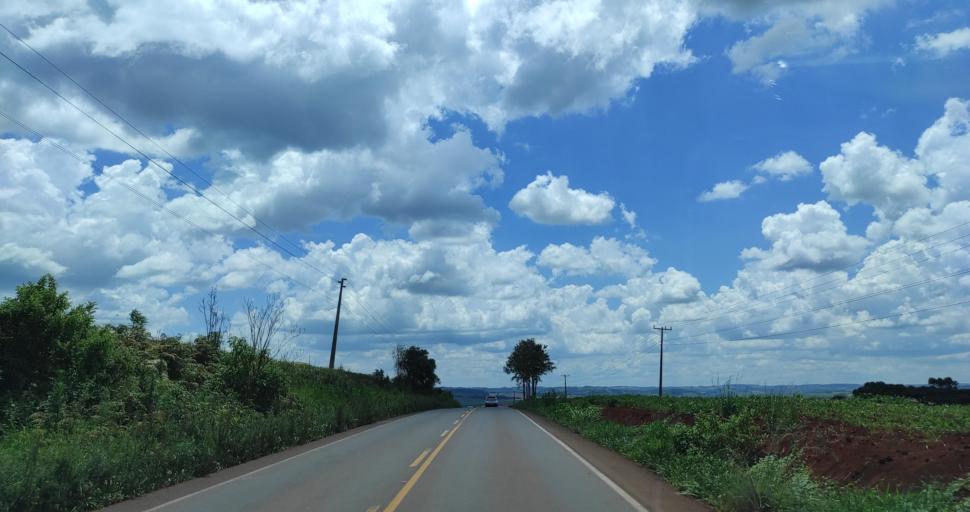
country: BR
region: Santa Catarina
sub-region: Xanxere
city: Xanxere
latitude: -26.7812
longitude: -52.4074
